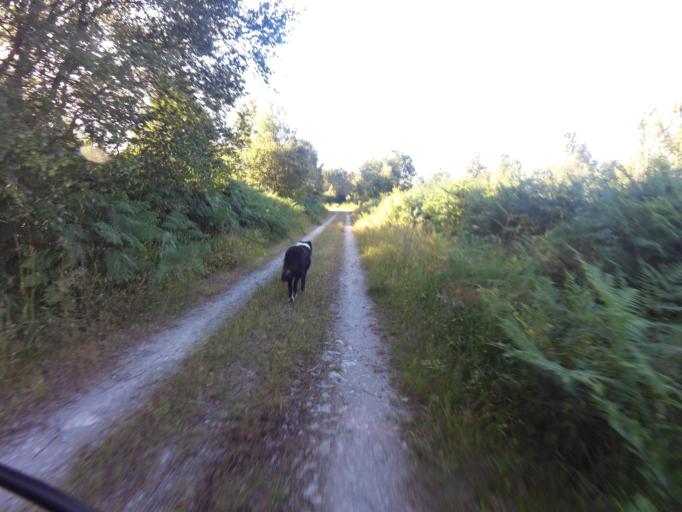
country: FR
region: Brittany
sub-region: Departement du Morbihan
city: Molac
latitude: 47.7551
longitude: -2.4308
